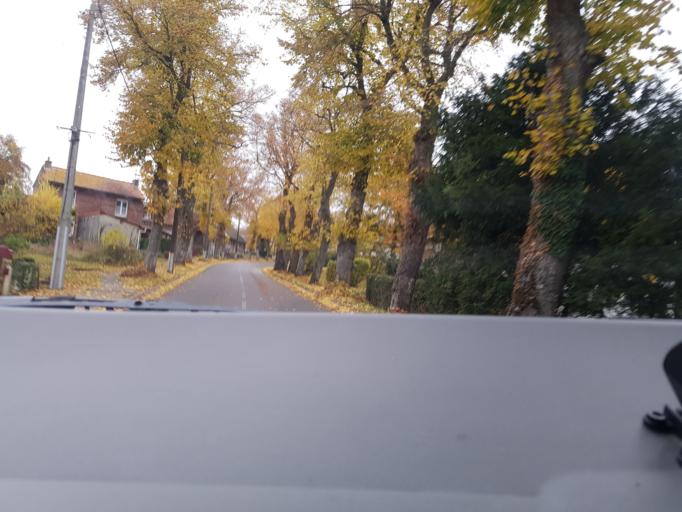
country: FR
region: Nord-Pas-de-Calais
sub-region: Departement du Pas-de-Calais
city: Auxi-le-Chateau
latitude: 50.2299
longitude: 2.1280
